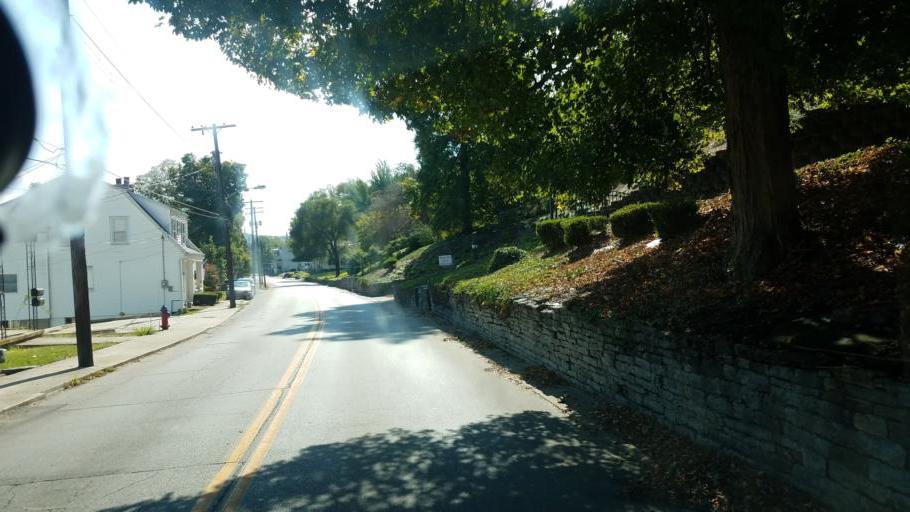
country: US
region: Ohio
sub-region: Brown County
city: Aberdeen
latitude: 38.6529
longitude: -83.7733
